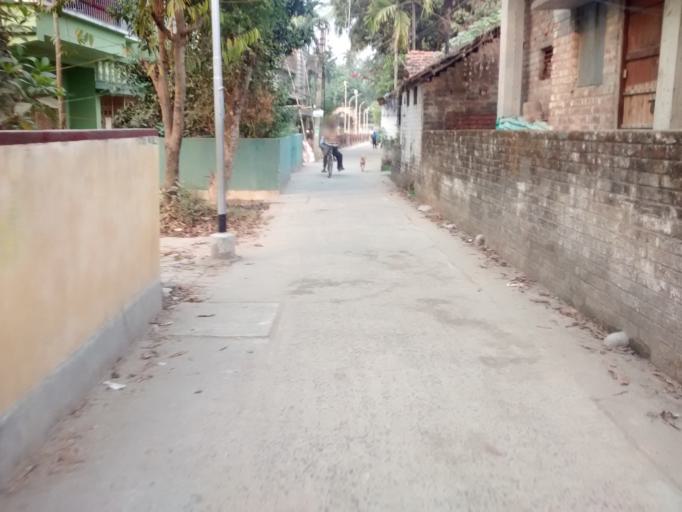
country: IN
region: West Bengal
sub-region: North 24 Parganas
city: Barasat
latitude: 22.7202
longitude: 88.4689
